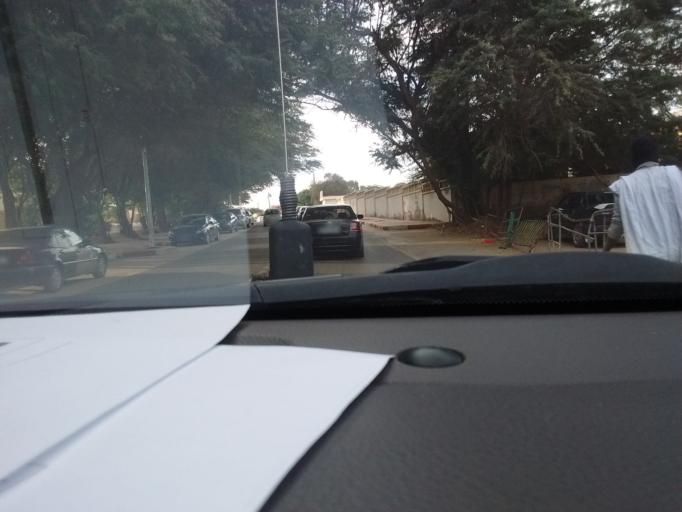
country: MR
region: Nouakchott
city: Nouakchott
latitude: 18.0916
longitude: -15.9835
